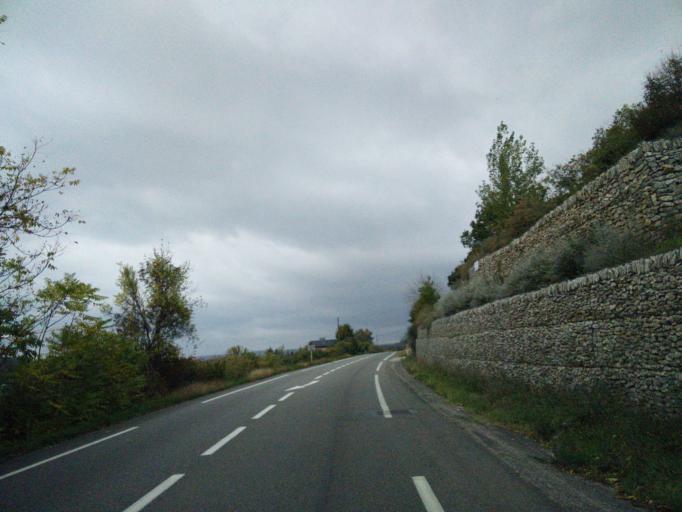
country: FR
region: Midi-Pyrenees
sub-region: Departement du Lot
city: Pradines
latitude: 44.4797
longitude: 1.4147
